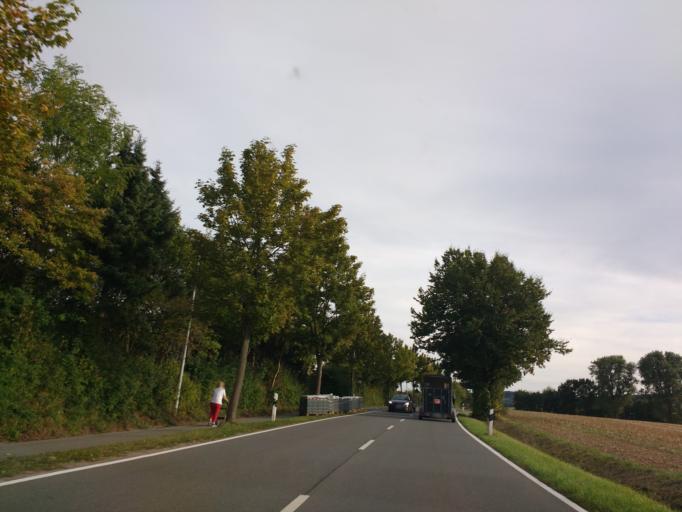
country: DE
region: North Rhine-Westphalia
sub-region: Regierungsbezirk Detmold
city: Bad Meinberg
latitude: 51.9382
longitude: 9.0239
